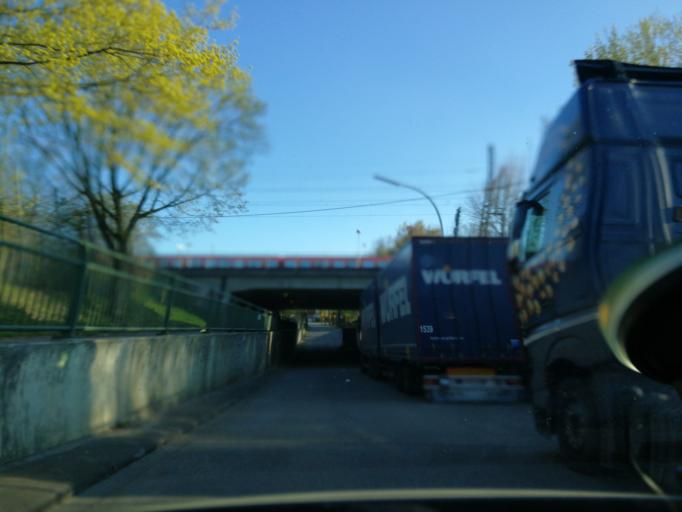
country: DE
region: Lower Saxony
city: Neu Wulmstorf
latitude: 53.4751
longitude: 9.8392
